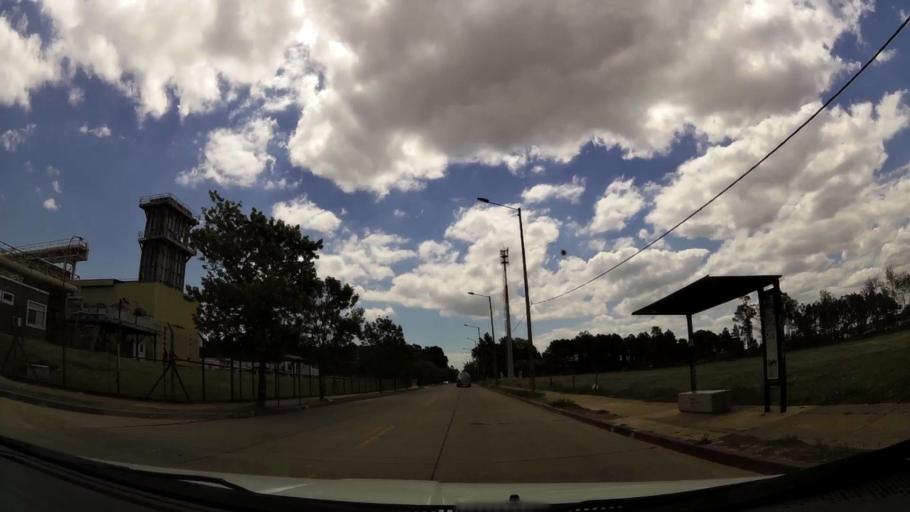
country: UY
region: Canelones
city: La Paz
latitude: -34.8263
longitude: -56.2356
